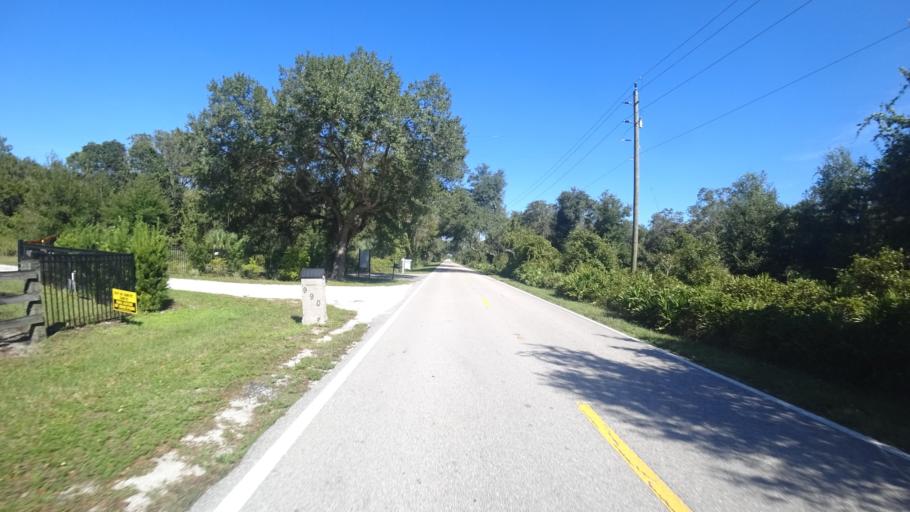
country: US
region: Florida
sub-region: Sarasota County
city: Lake Sarasota
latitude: 27.3239
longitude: -82.2693
